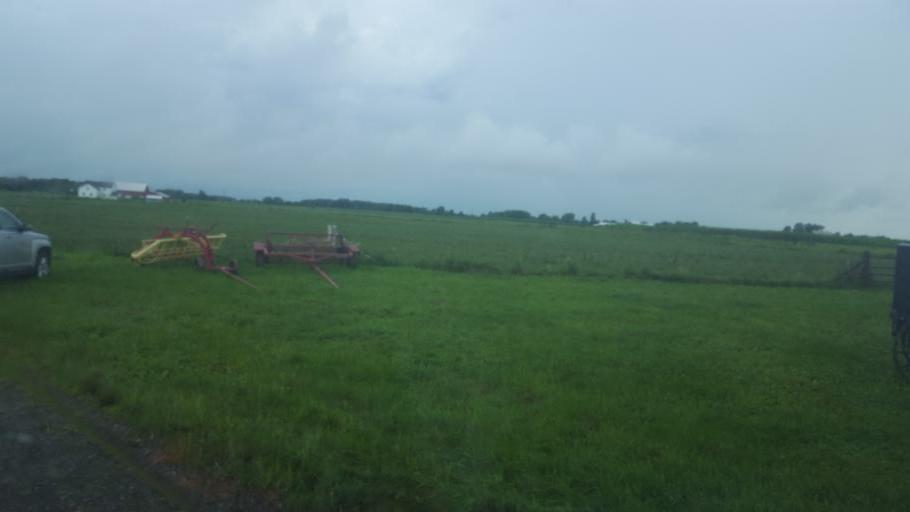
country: US
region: Ohio
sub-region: Union County
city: Richwood
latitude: 40.5588
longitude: -83.4124
